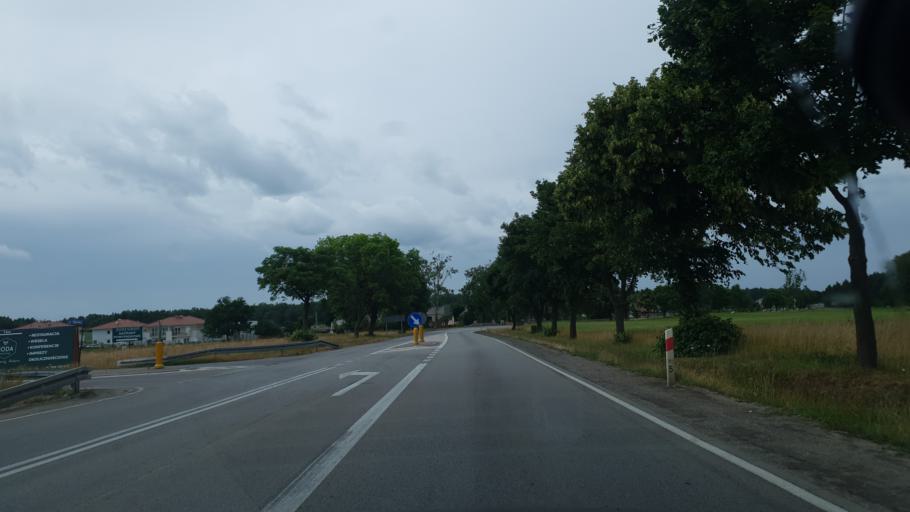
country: PL
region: Pomeranian Voivodeship
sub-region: Powiat kartuski
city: Banino
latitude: 54.3922
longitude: 18.3577
